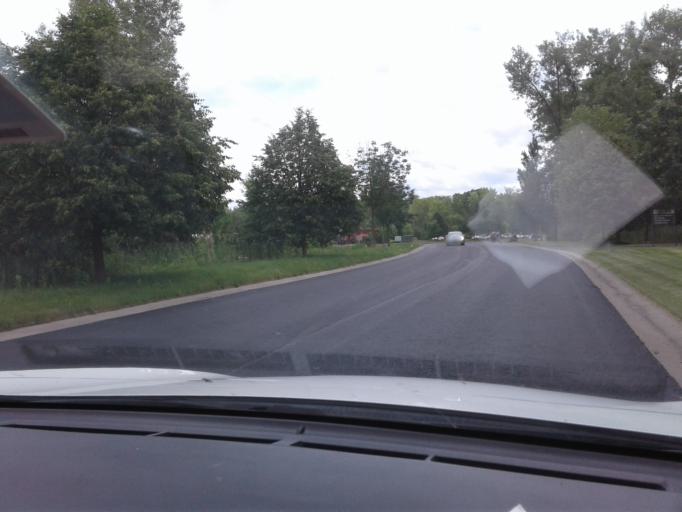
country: US
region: New York
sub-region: Onondaga County
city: East Syracuse
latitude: 43.0879
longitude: -76.0750
